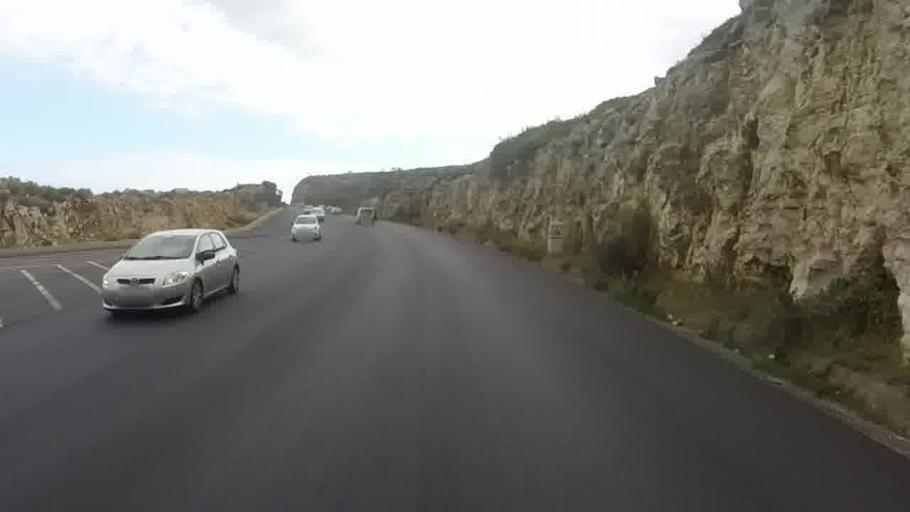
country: GR
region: Crete
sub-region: Nomos Rethymnis
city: Atsipopoulon
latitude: 35.3585
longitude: 24.4092
